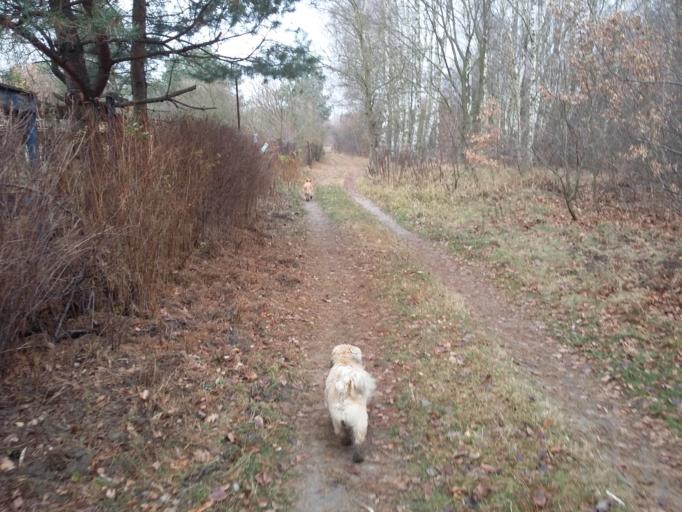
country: PL
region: Lodz Voivodeship
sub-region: Powiat pabianicki
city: Ksawerow
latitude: 51.7301
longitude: 19.4116
